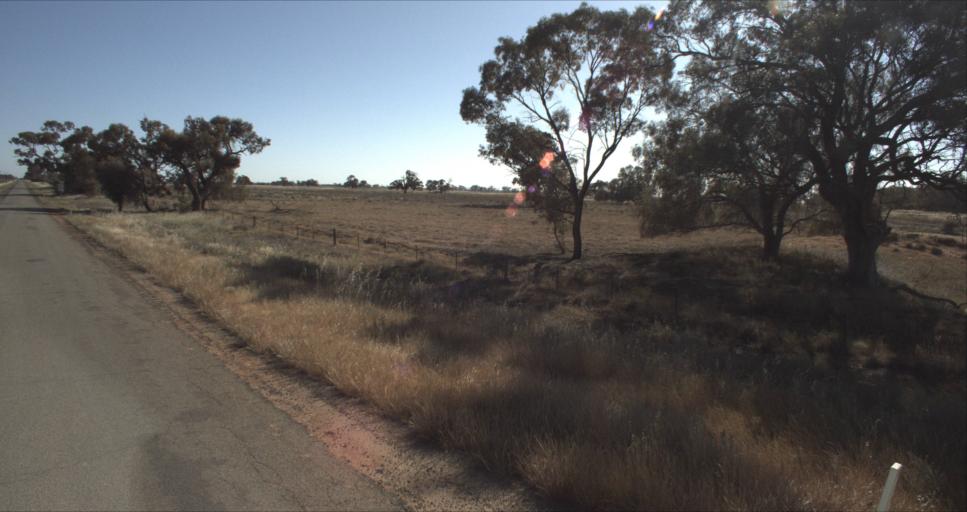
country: AU
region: New South Wales
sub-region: Leeton
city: Leeton
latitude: -34.6048
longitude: 146.2570
